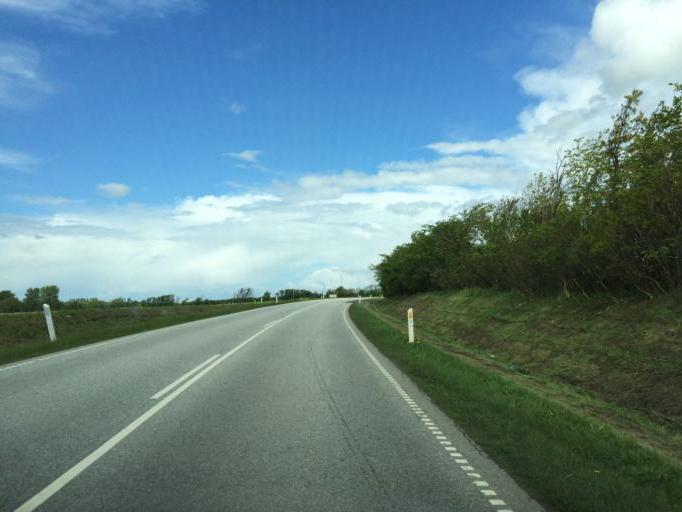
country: DK
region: North Denmark
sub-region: Vesthimmerland Kommune
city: Farso
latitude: 56.8268
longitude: 9.3704
